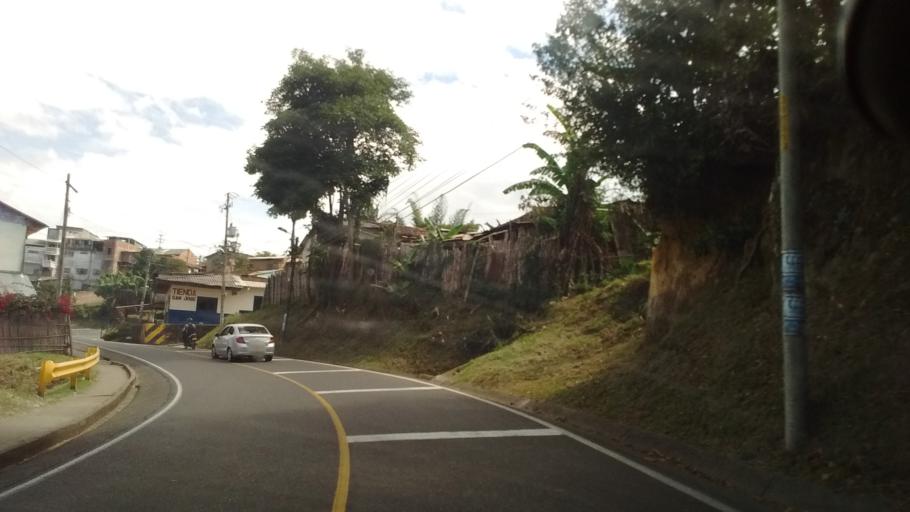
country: CO
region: Cauca
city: Cajibio
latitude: 2.6375
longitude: -76.5275
